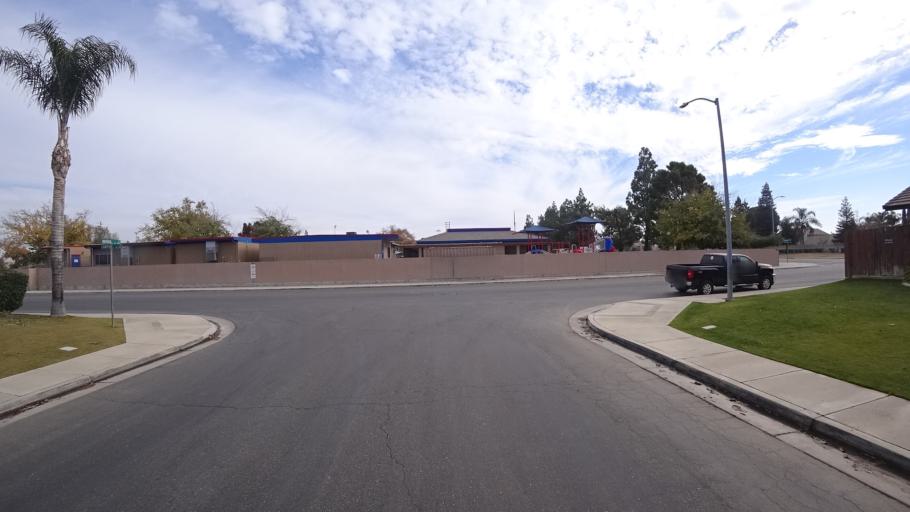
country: US
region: California
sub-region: Kern County
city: Rosedale
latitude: 35.3914
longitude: -119.1310
